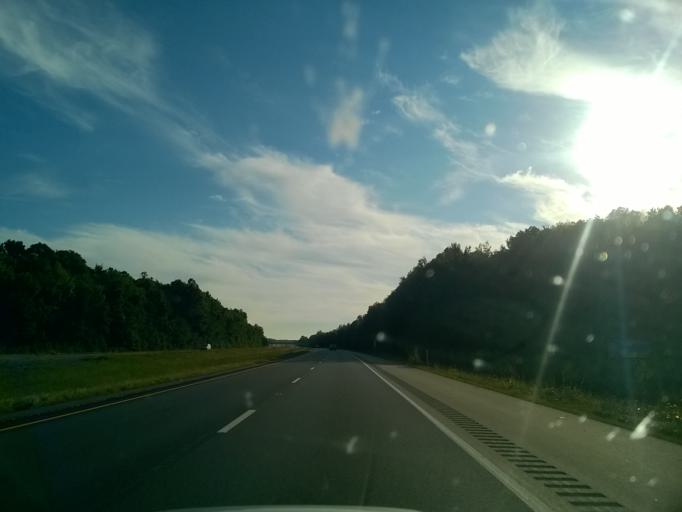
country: US
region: Indiana
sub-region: Warrick County
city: Chandler
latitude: 38.1853
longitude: -87.3611
